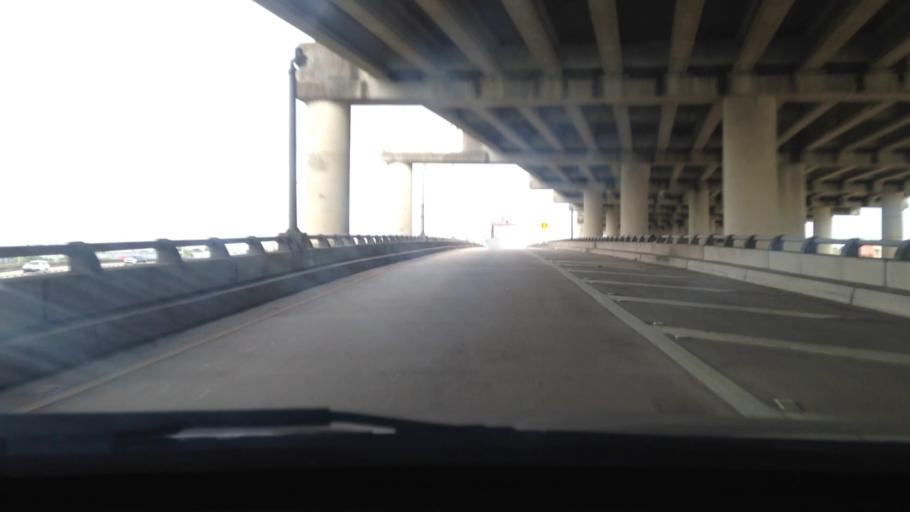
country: US
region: Louisiana
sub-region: Orleans Parish
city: New Orleans
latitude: 29.9663
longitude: -90.1060
